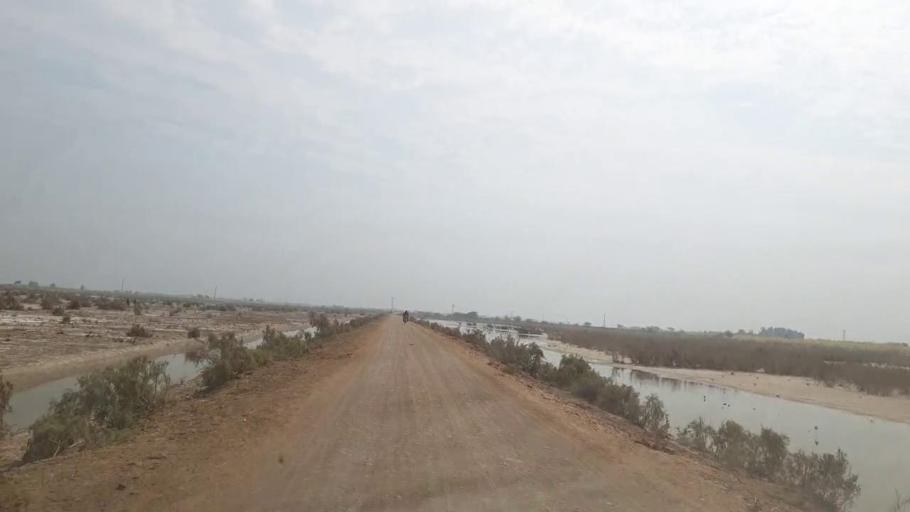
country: PK
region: Sindh
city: Mirpur Khas
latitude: 25.5550
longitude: 69.1216
